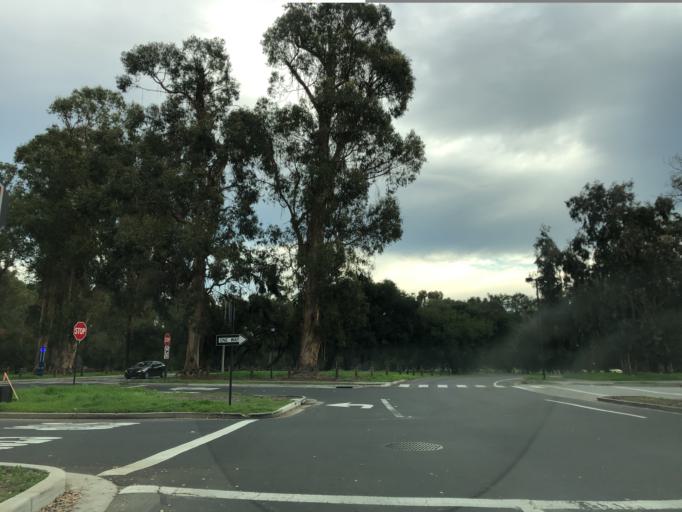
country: US
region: California
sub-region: Santa Clara County
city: Stanford
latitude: 37.4340
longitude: -122.1726
